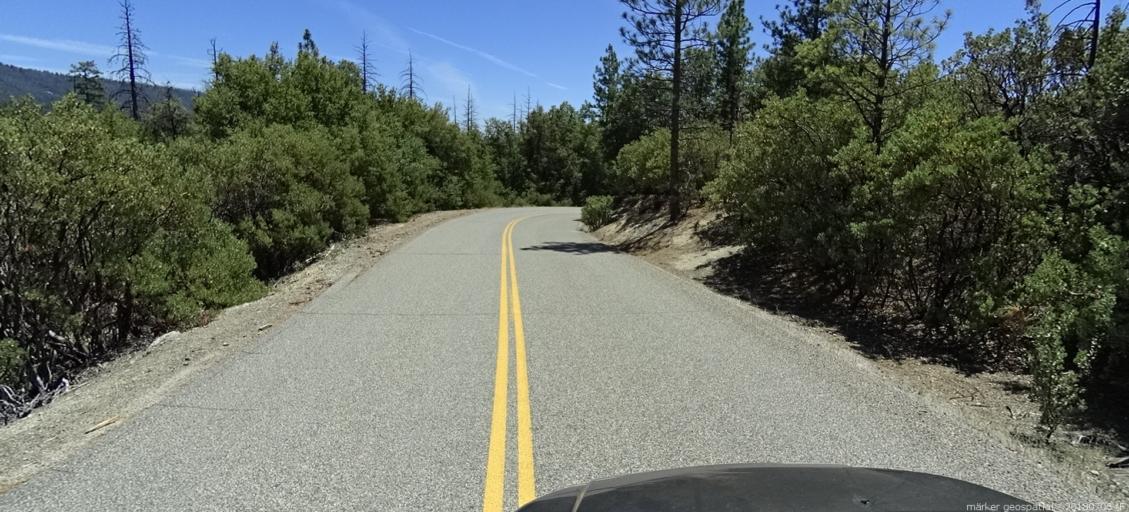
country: US
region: California
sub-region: Madera County
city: Oakhurst
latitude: 37.3339
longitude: -119.5575
